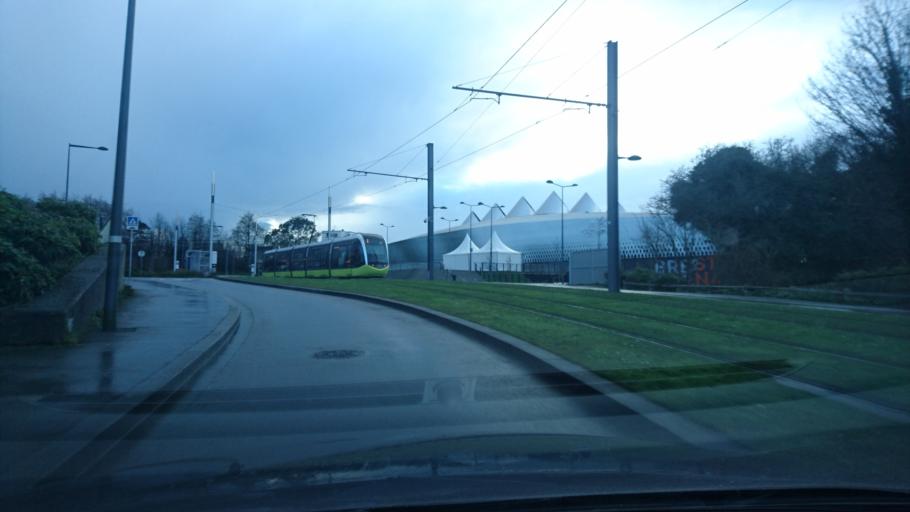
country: FR
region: Brittany
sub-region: Departement du Finistere
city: Brest
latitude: 48.3877
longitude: -4.5180
